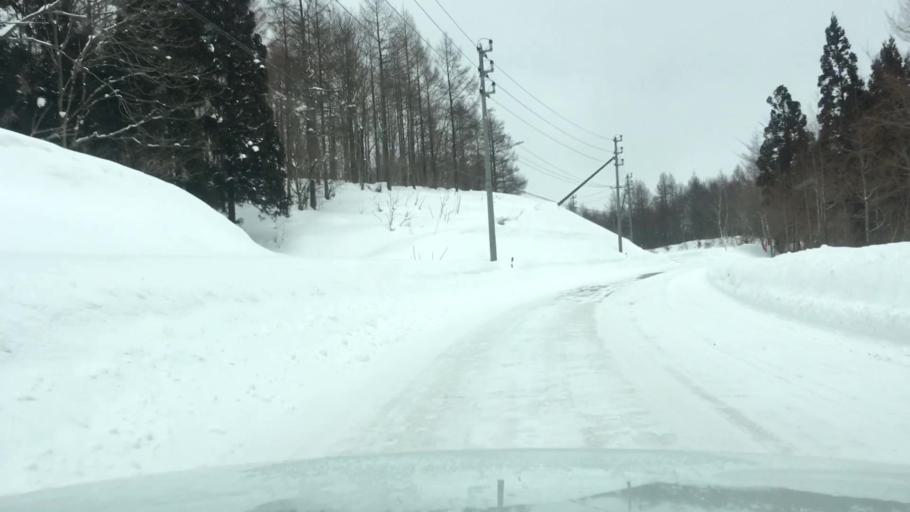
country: JP
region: Akita
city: Hanawa
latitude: 40.0007
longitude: 140.9859
